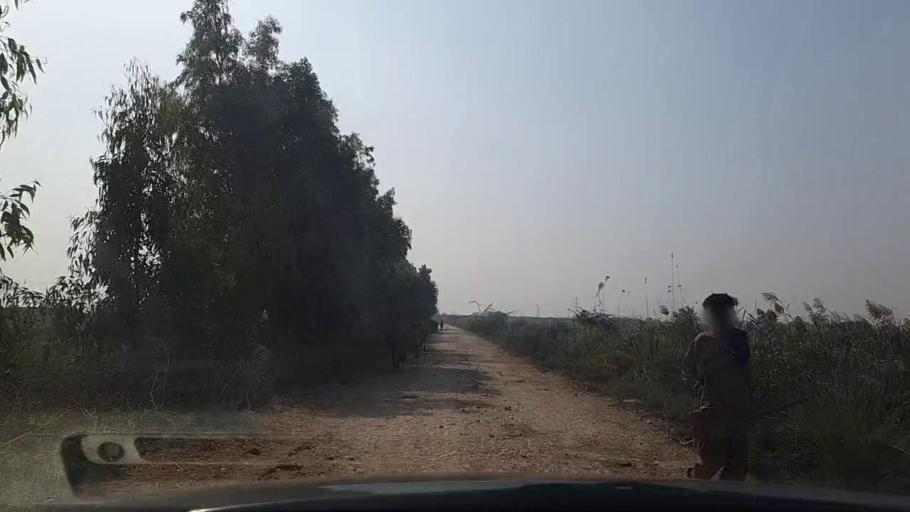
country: PK
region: Sindh
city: Mirpur Sakro
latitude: 24.5720
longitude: 67.7793
